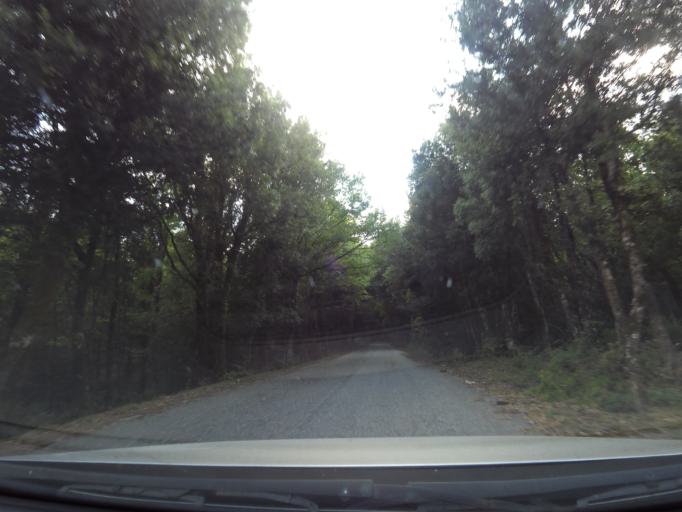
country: IT
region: Calabria
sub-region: Provincia di Vibo-Valentia
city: Nardodipace
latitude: 38.5056
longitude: 16.3812
